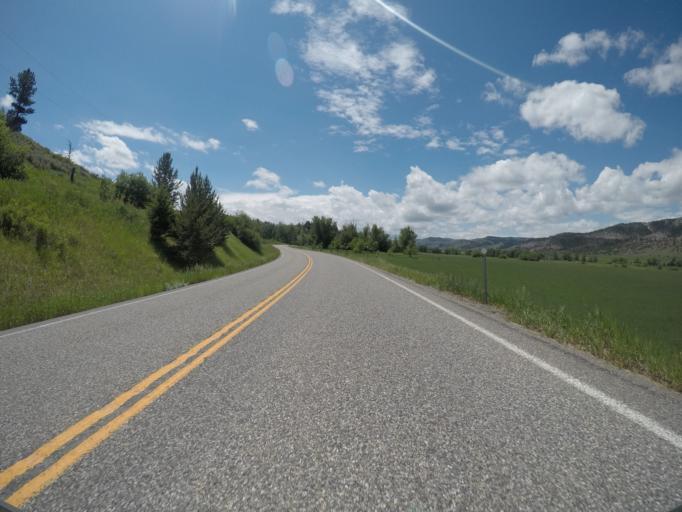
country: US
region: Montana
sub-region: Sweet Grass County
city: Big Timber
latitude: 45.6982
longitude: -110.0212
